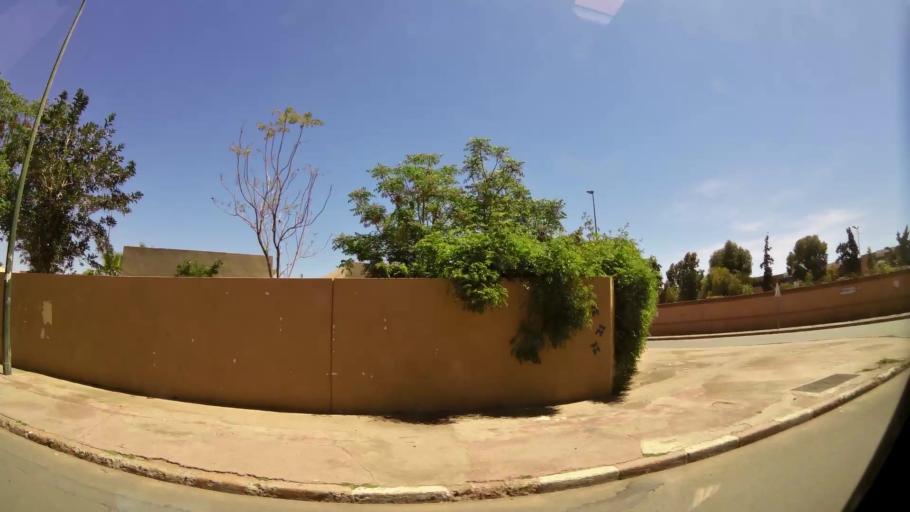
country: MA
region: Marrakech-Tensift-Al Haouz
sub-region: Marrakech
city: Marrakesh
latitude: 31.6450
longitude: -7.9986
